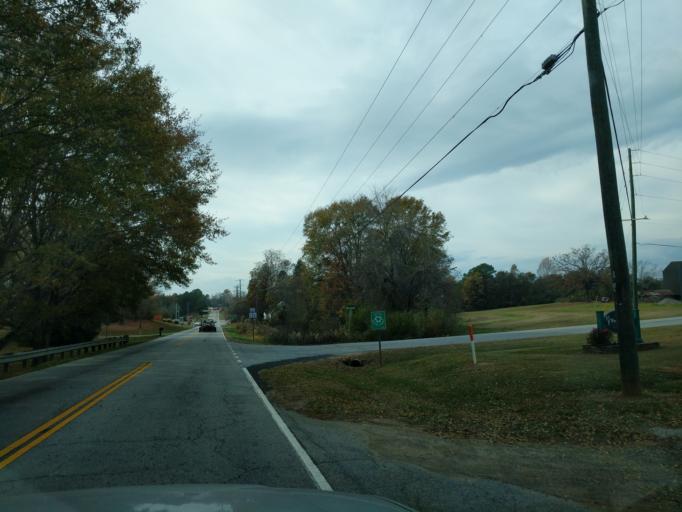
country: US
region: South Carolina
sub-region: Pickens County
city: Central
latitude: 34.8323
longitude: -82.8372
